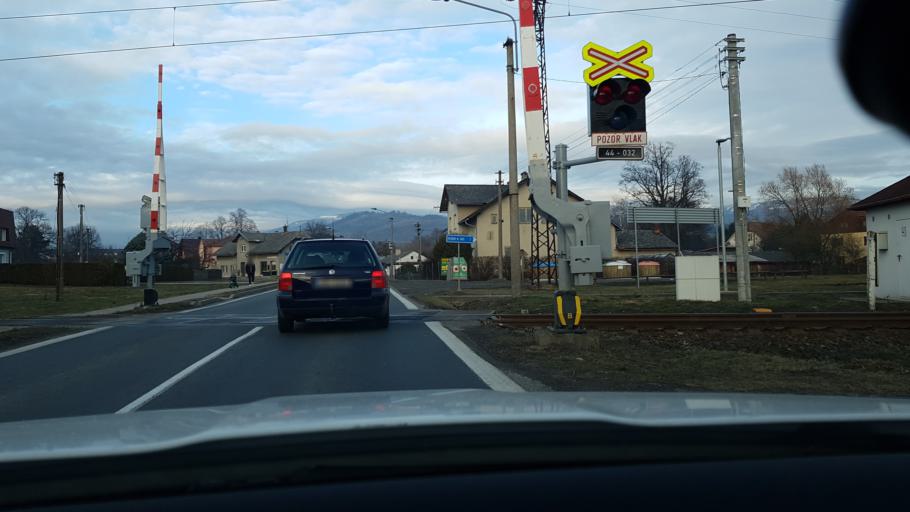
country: CZ
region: Olomoucky
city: Rapotin
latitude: 50.0096
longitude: 17.0308
